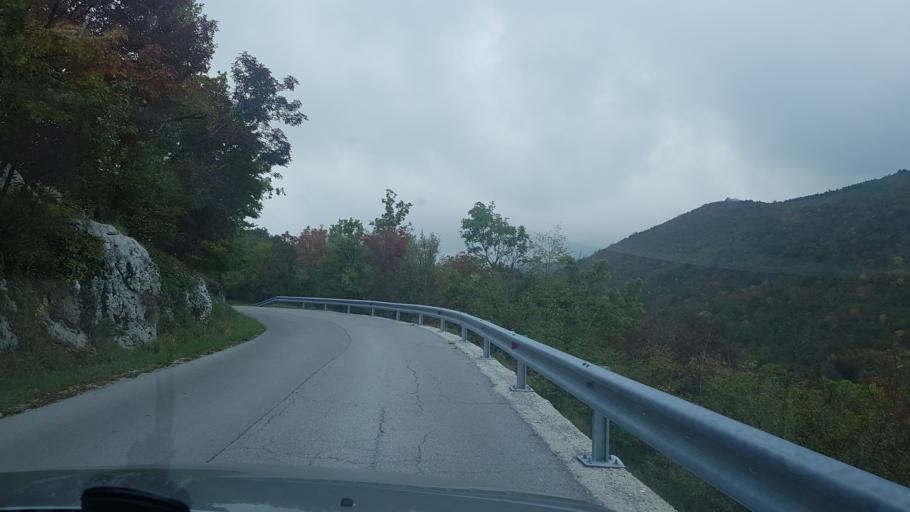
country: SI
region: Hrpelje-Kozina
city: Kozina
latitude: 45.5149
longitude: 13.9597
